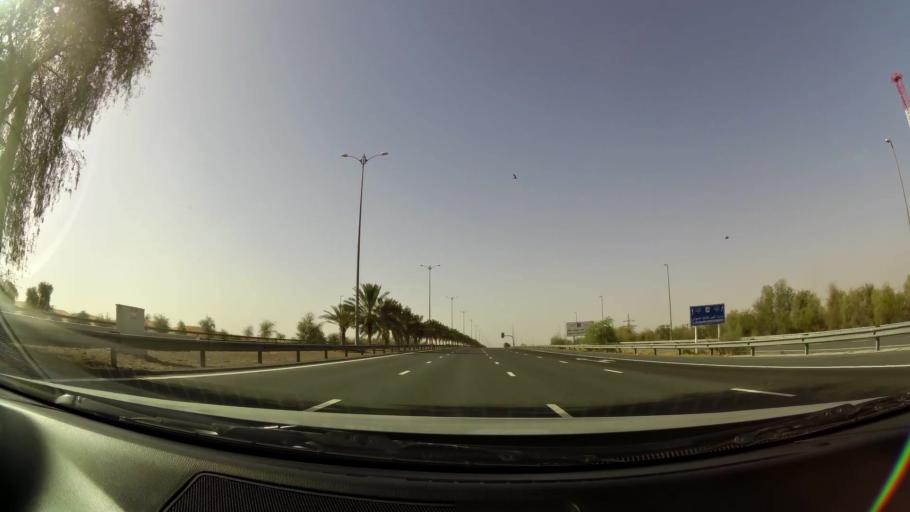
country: OM
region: Al Buraimi
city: Al Buraymi
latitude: 24.4158
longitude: 55.7923
